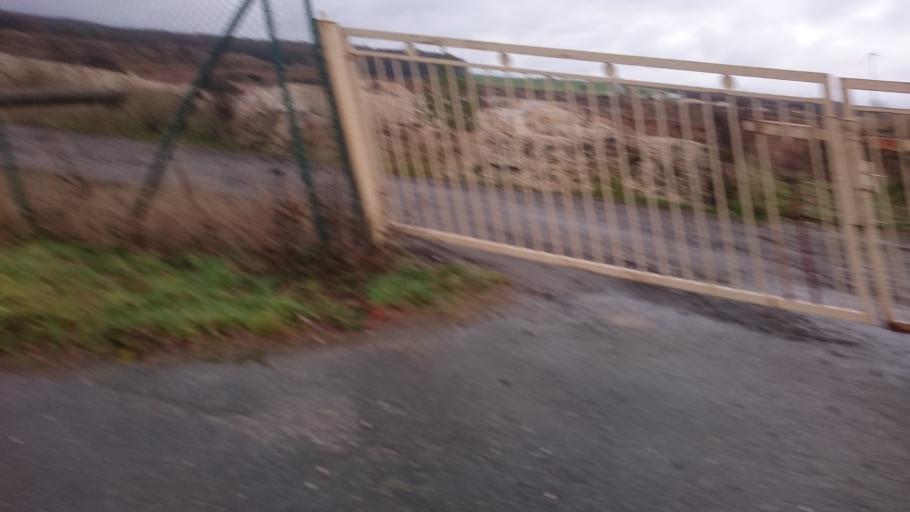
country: DE
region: Saxony
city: Mulsen
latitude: 50.7421
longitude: 12.5316
